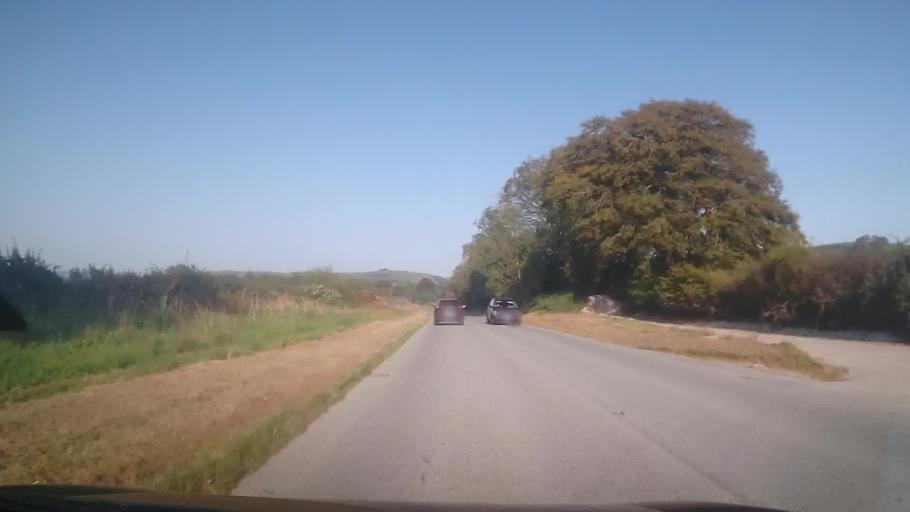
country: GB
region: Wales
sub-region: County of Ceredigion
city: Lledrod
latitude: 52.2106
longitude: -3.9498
